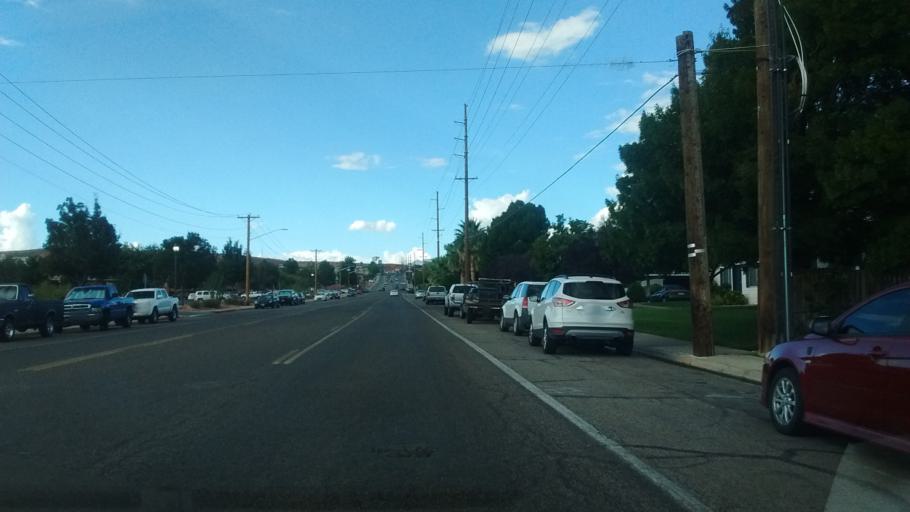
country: US
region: Utah
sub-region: Washington County
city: Saint George
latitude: 37.1030
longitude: -113.5621
